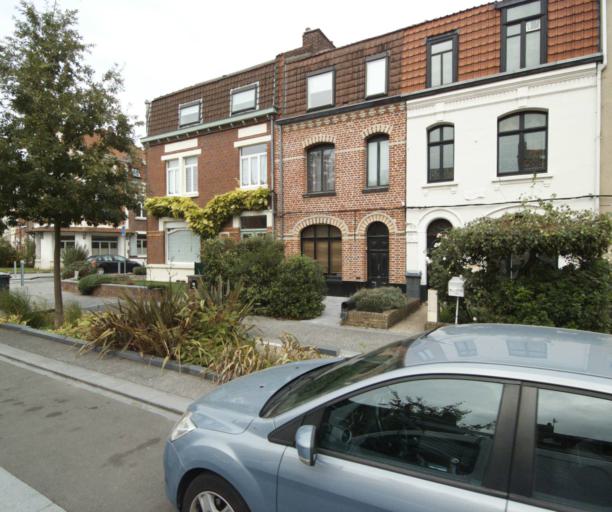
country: FR
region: Nord-Pas-de-Calais
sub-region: Departement du Nord
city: Lambersart
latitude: 50.6461
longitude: 3.0309
